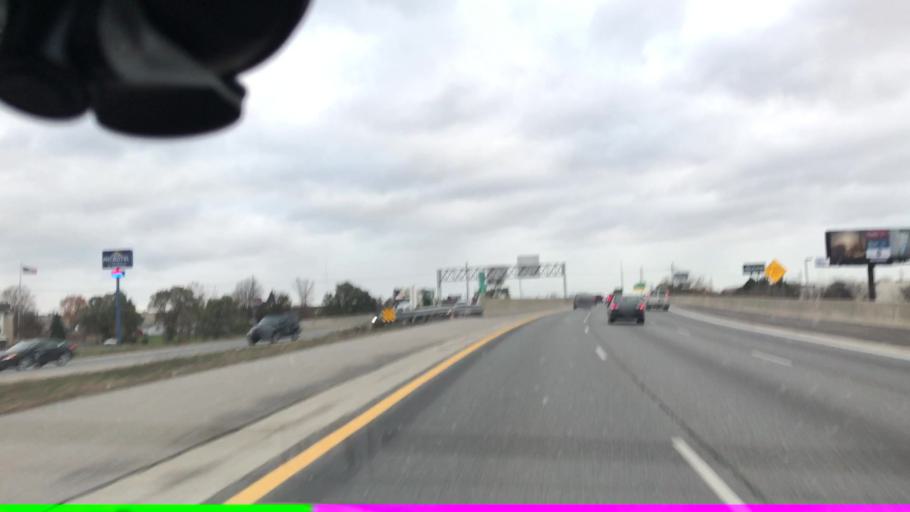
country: US
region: Michigan
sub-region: Macomb County
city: Roseville
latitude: 42.5233
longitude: -82.9139
